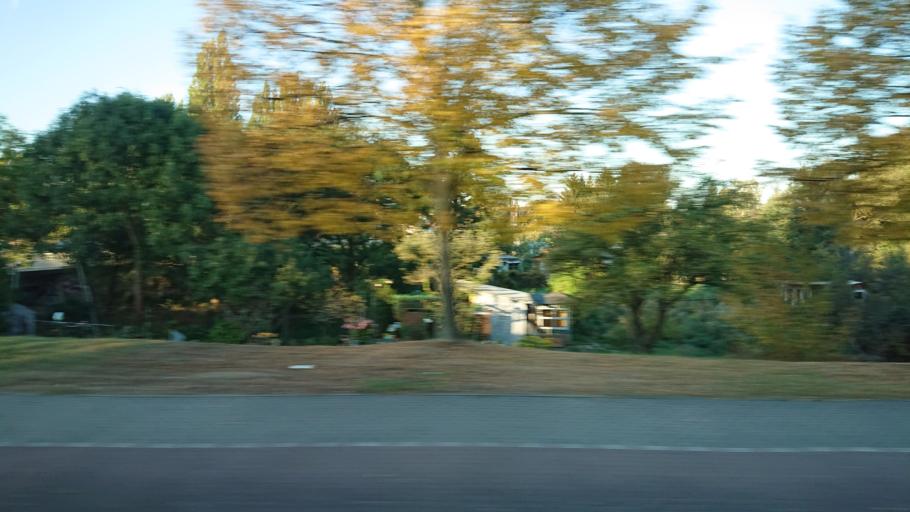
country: DE
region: Mecklenburg-Vorpommern
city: Neubrandenburg
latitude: 53.5718
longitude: 13.2691
